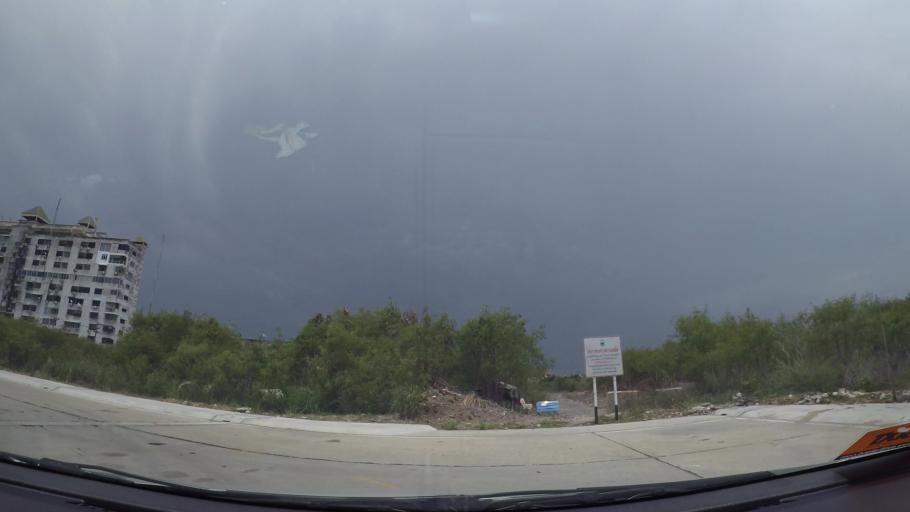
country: TH
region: Chon Buri
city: Chon Buri
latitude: 13.3440
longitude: 100.9562
